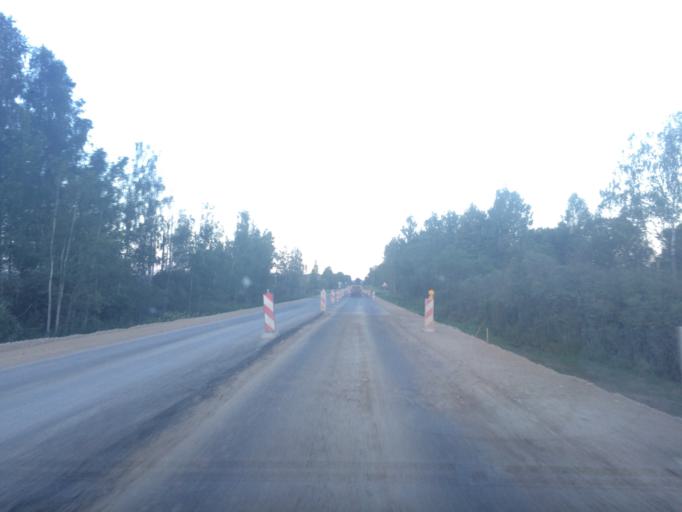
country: LT
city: Zarasai
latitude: 55.7507
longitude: 26.3186
